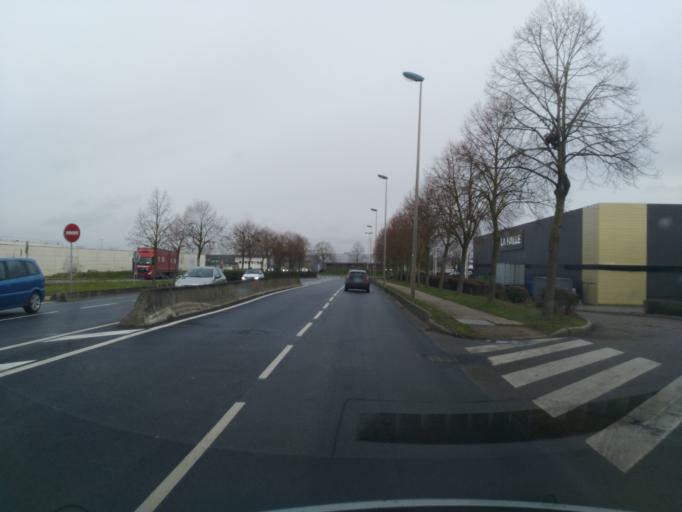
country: FR
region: Ile-de-France
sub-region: Departement des Yvelines
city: Plaisir
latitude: 48.8283
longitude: 1.9639
